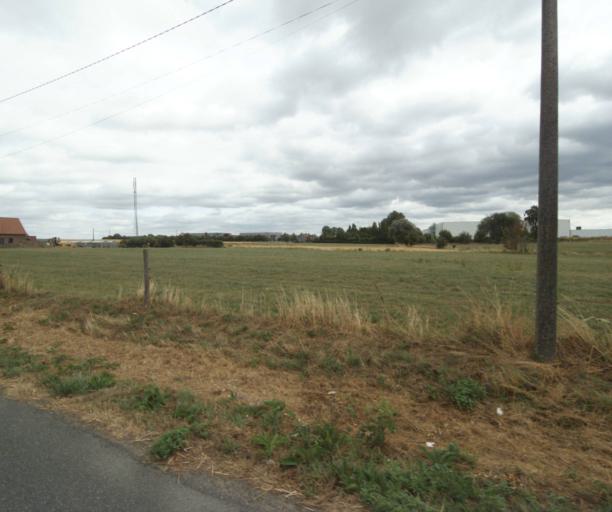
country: FR
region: Nord-Pas-de-Calais
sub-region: Departement du Nord
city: Linselles
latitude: 50.7467
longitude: 3.0784
